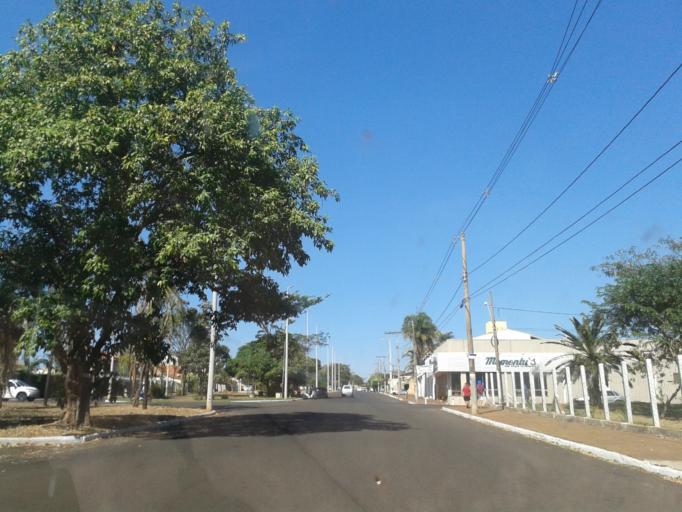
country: BR
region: Minas Gerais
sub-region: Ituiutaba
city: Ituiutaba
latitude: -18.9846
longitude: -49.4626
